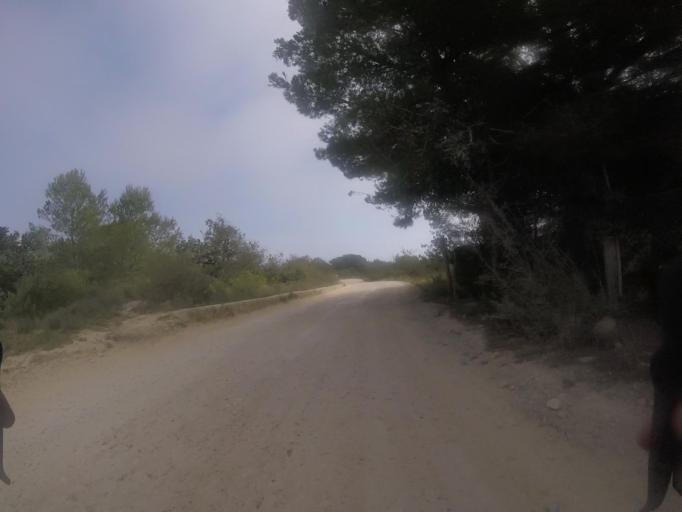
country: ES
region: Valencia
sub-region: Provincia de Castello
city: Alcoceber
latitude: 40.2595
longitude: 0.2964
